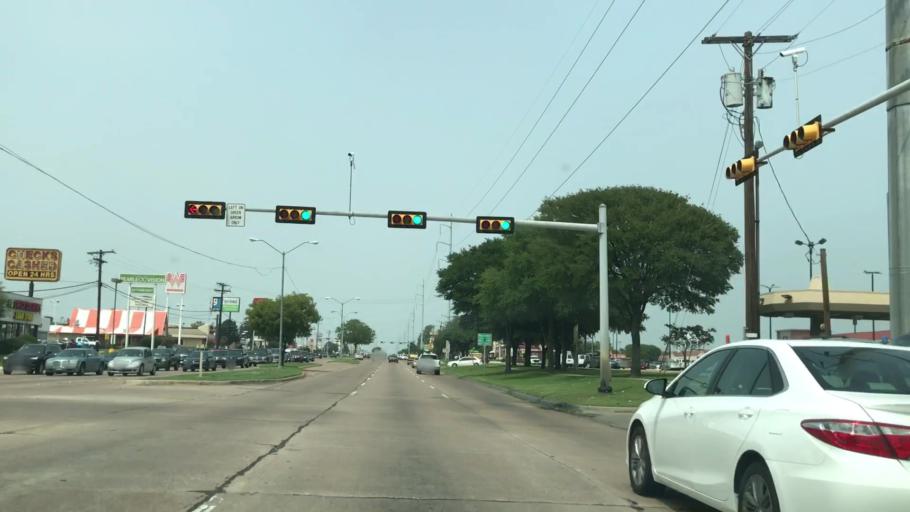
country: US
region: Texas
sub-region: Dallas County
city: Irving
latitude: 32.8448
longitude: -96.9923
